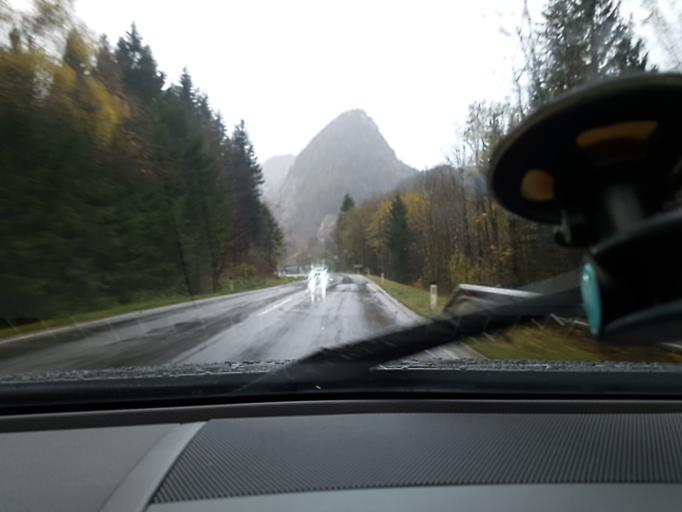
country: AT
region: Styria
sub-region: Politischer Bezirk Liezen
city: Ardning
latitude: 47.6295
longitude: 14.3219
